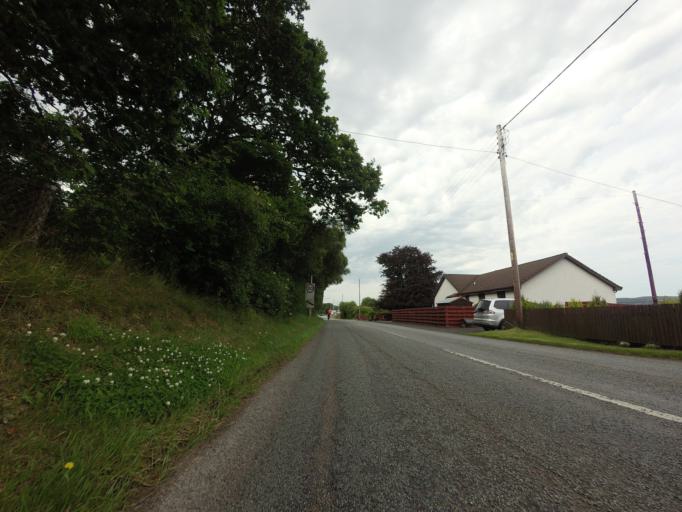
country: GB
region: Scotland
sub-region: Highland
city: Alness
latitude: 57.8784
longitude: -4.3598
